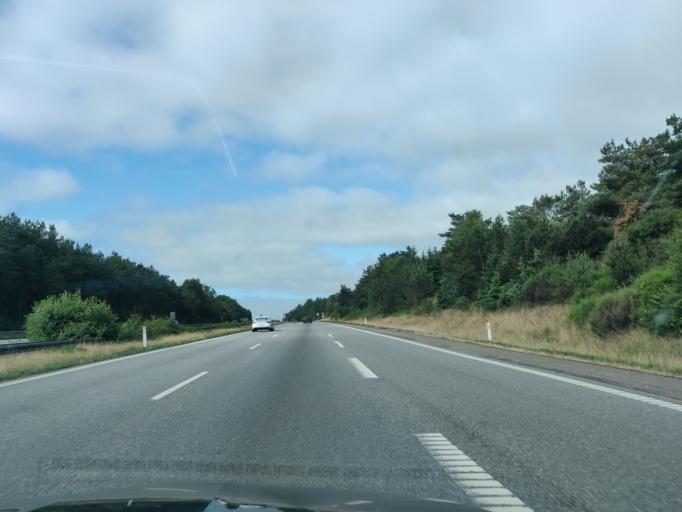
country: DK
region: North Denmark
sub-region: Rebild Kommune
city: Stovring
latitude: 56.9019
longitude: 9.8292
